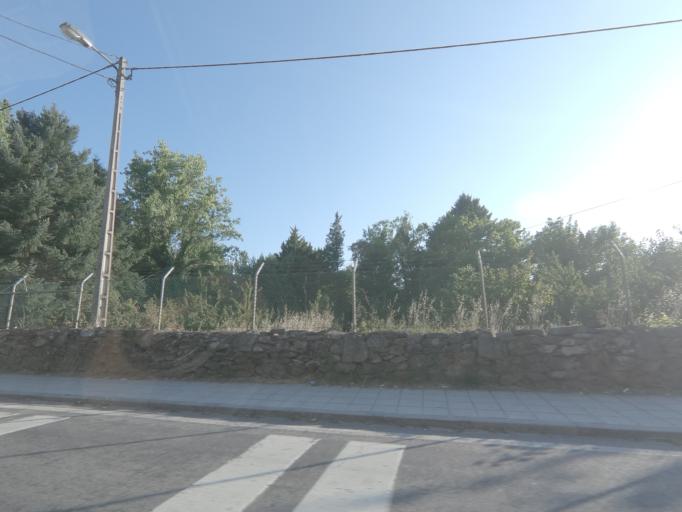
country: PT
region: Vila Real
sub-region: Vila Real
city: Vila Real
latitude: 41.2982
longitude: -7.7140
